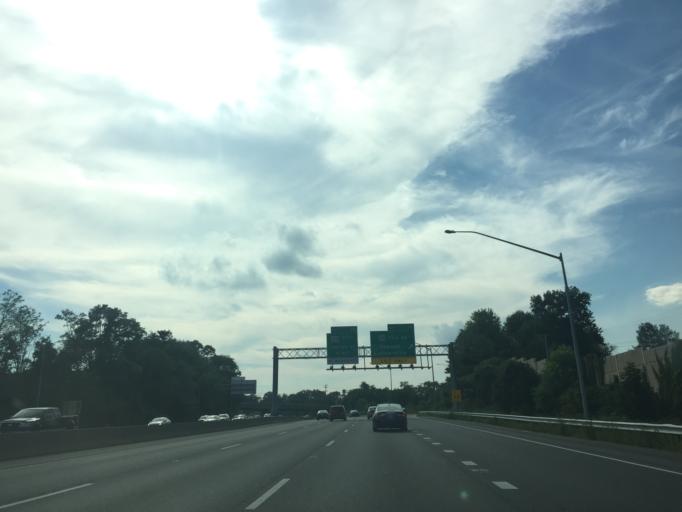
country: US
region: Maryland
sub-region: Baltimore County
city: Towson
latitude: 39.4138
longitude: -76.6078
